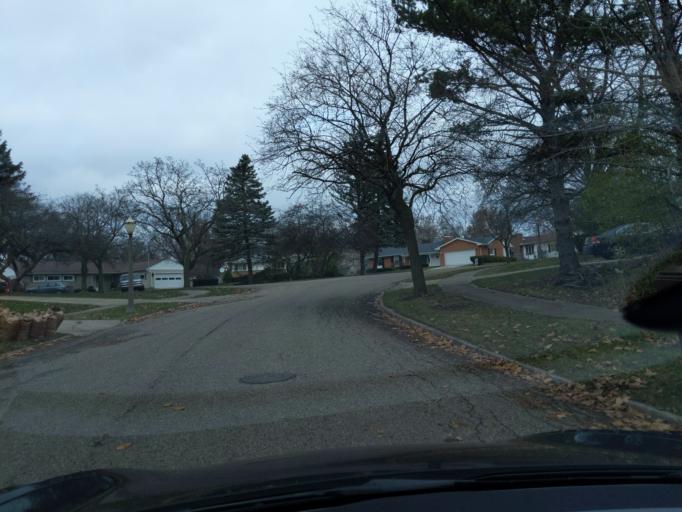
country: US
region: Michigan
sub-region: Ingham County
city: Edgemont Park
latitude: 42.7098
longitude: -84.5861
